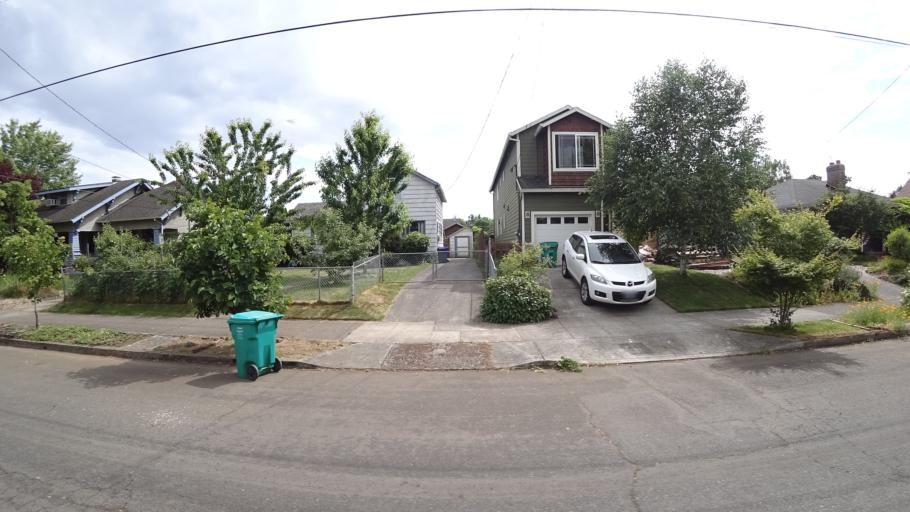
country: US
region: Oregon
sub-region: Washington County
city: West Haven
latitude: 45.5862
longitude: -122.7416
